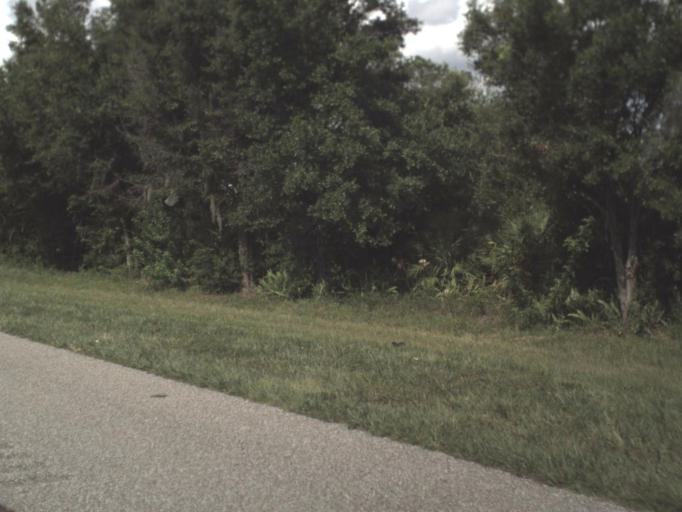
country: US
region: Florida
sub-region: Hillsborough County
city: Apollo Beach
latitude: 27.7606
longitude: -82.3707
